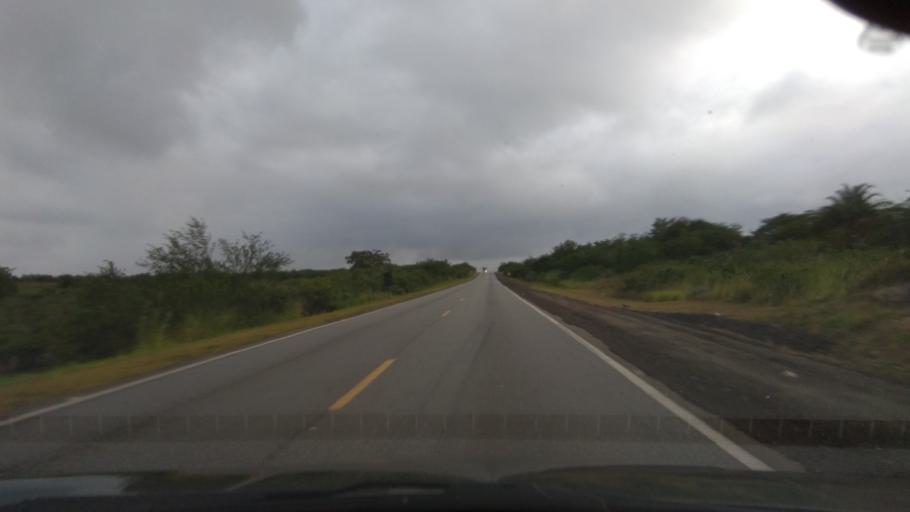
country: BR
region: Bahia
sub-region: Jaguaquara
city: Jaguaquara
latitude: -13.4173
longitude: -40.0264
